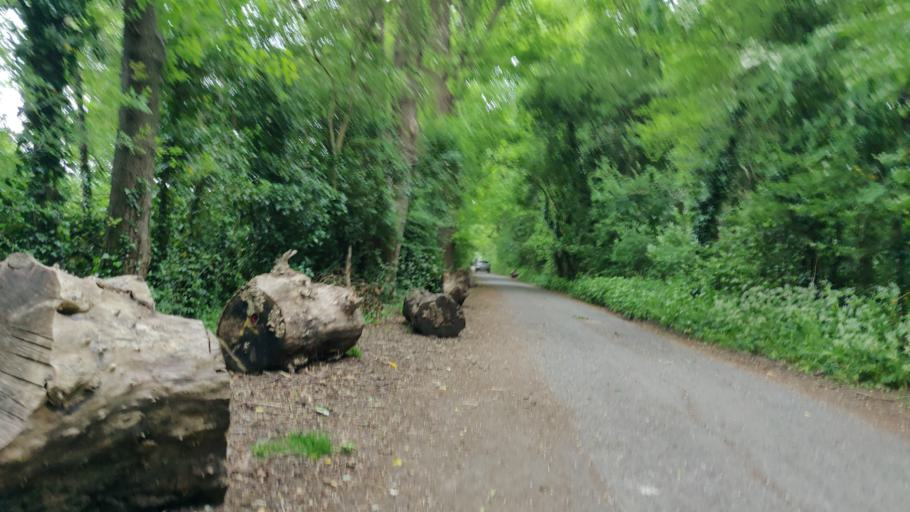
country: GB
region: England
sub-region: West Sussex
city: Southwater
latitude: 51.0204
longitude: -0.3447
